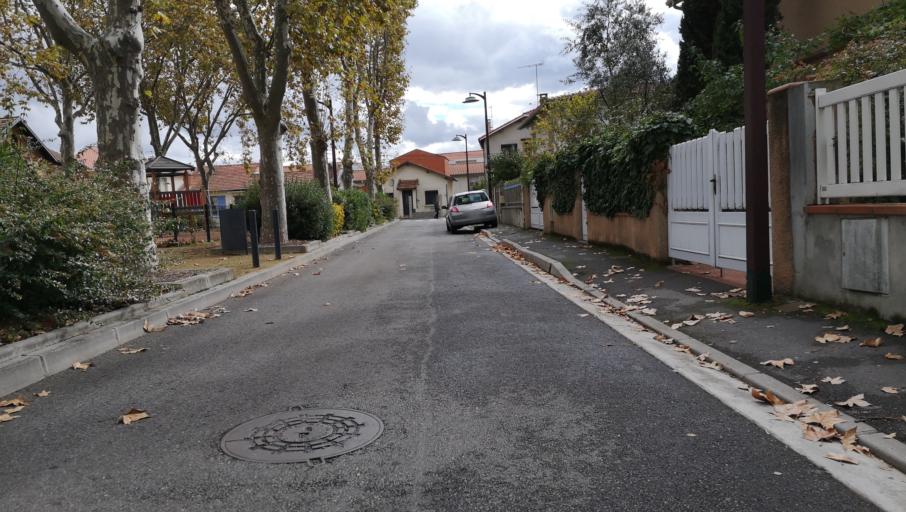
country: FR
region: Midi-Pyrenees
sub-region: Departement de la Haute-Garonne
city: Toulouse
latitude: 43.6051
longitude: 1.4120
